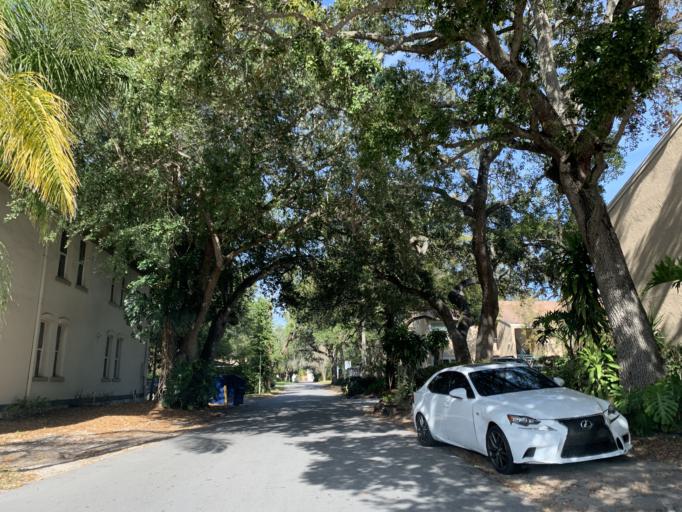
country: US
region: Florida
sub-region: Hillsborough County
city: Tampa
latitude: 27.8938
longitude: -82.4986
